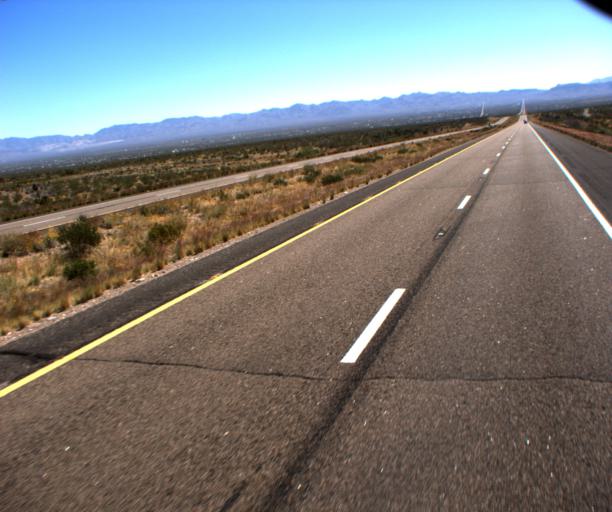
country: US
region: Arizona
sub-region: Mohave County
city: Golden Valley
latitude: 35.2285
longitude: -114.3531
